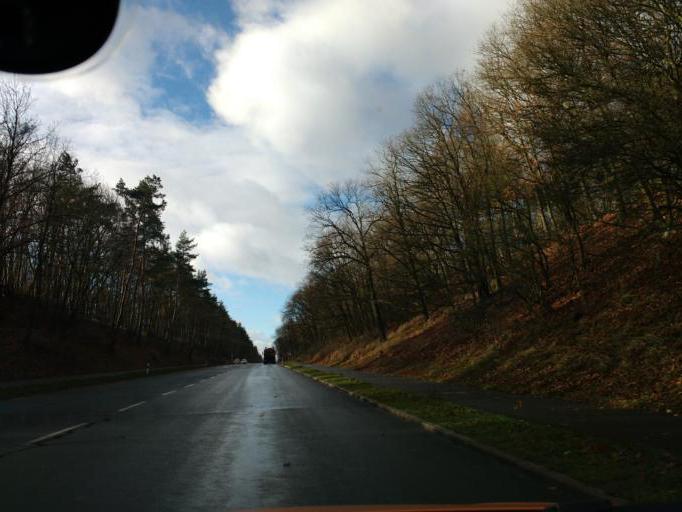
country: DE
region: Berlin
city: Wannsee
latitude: 52.4160
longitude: 13.1286
